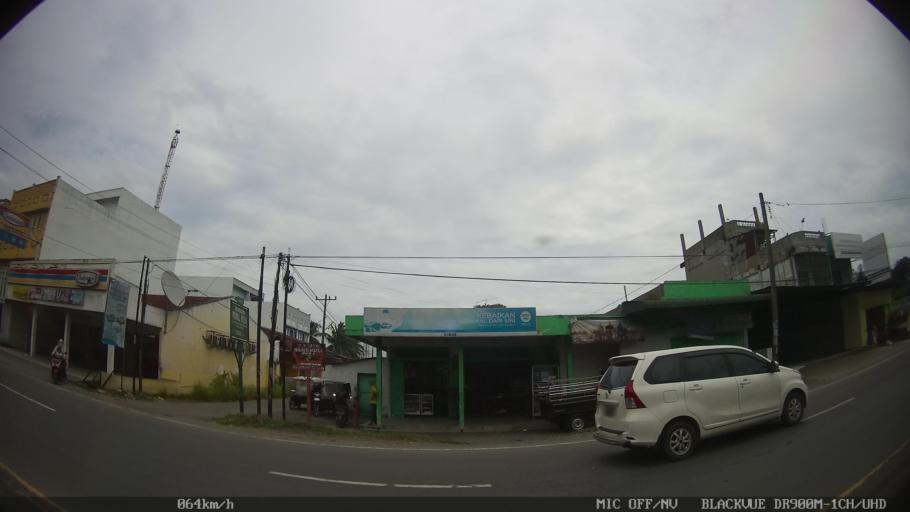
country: ID
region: North Sumatra
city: Sunggal
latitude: 3.5995
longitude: 98.5682
